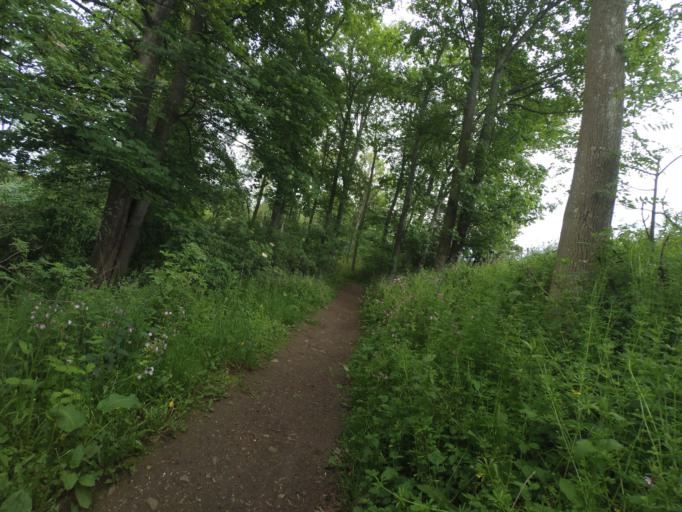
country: GB
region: Scotland
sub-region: East Lothian
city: Pencaitland
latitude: 55.9121
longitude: -2.9135
